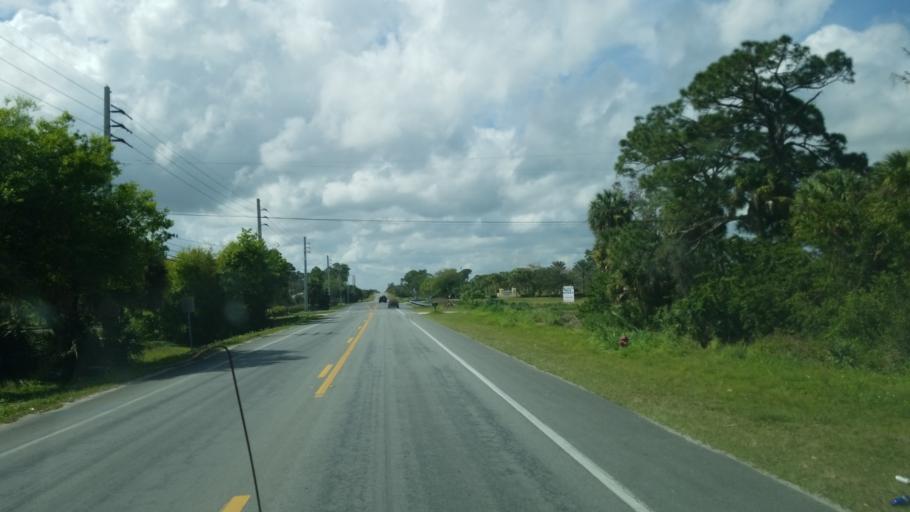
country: US
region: Florida
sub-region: Saint Lucie County
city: Lakewood Park
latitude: 27.4475
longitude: -80.4191
